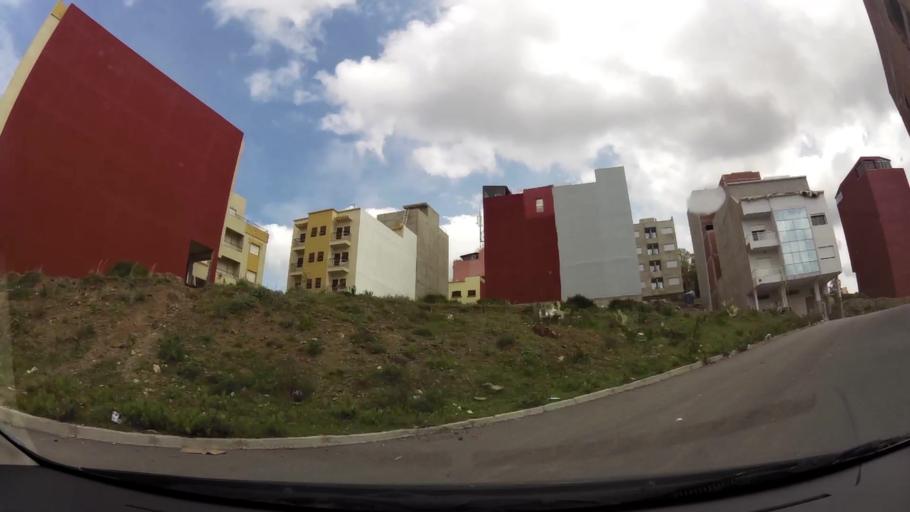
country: MA
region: Tanger-Tetouan
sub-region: Tanger-Assilah
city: Tangier
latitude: 35.7704
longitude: -5.7553
